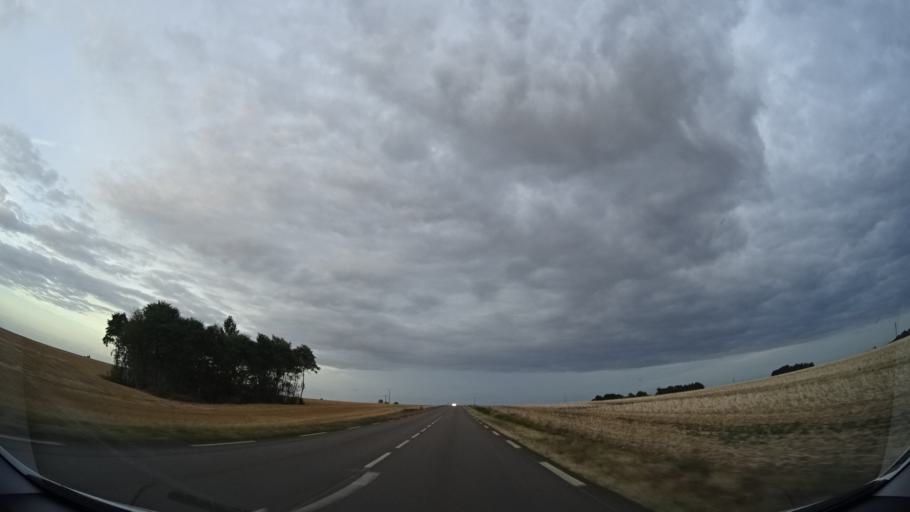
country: FR
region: Bourgogne
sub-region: Departement de l'Yonne
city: Charny
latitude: 47.9313
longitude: 3.1760
